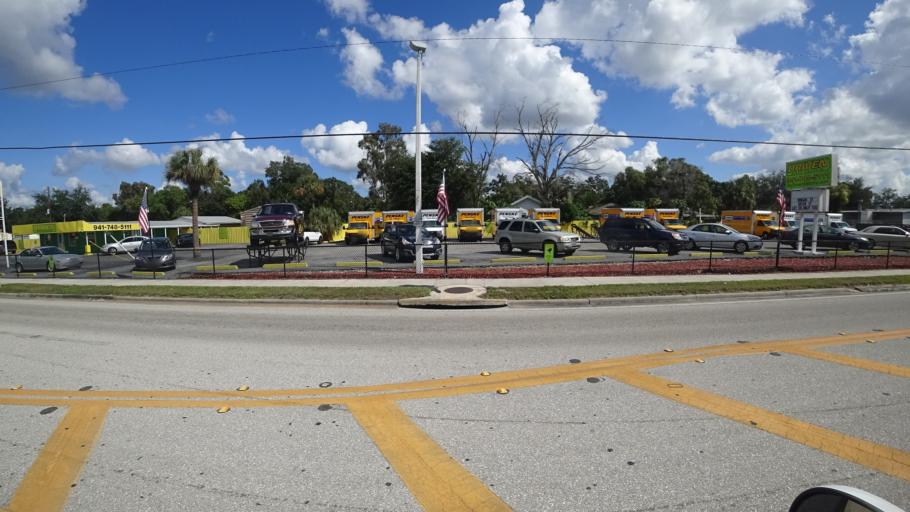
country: US
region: Florida
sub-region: Manatee County
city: West Samoset
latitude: 27.4753
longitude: -82.5712
